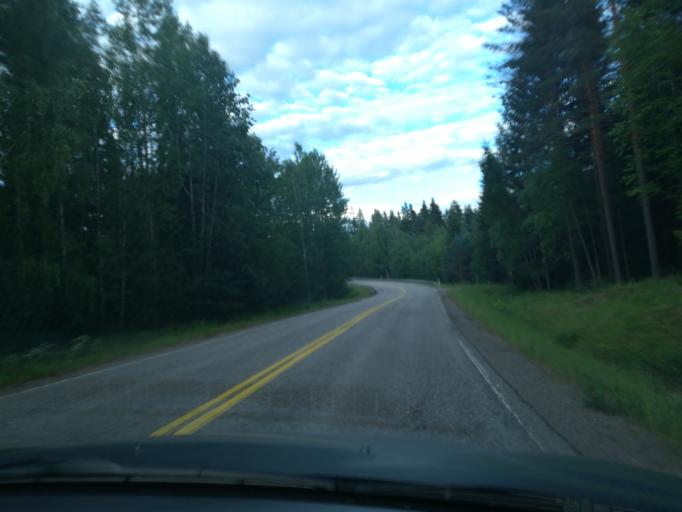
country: FI
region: Southern Savonia
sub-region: Mikkeli
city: Puumala
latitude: 61.5274
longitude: 27.9409
